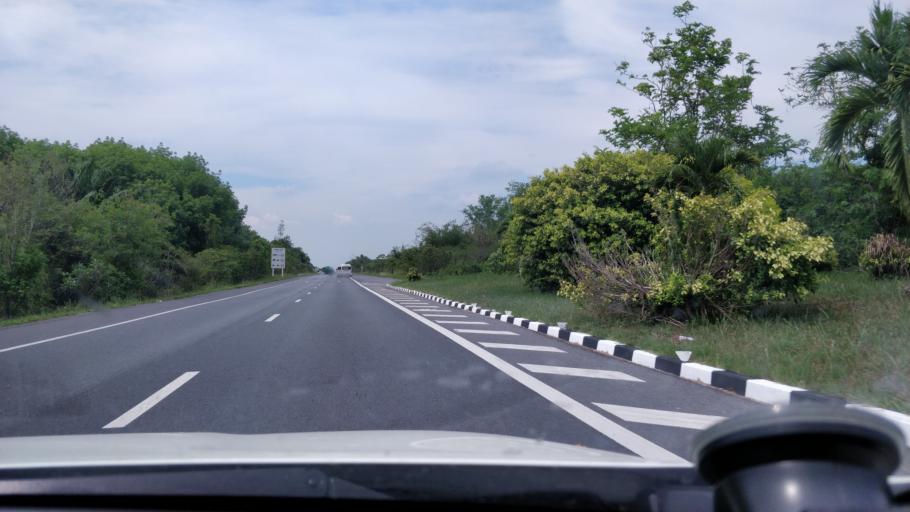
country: TH
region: Surat Thani
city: Khian Sa
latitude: 8.8251
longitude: 99.1713
